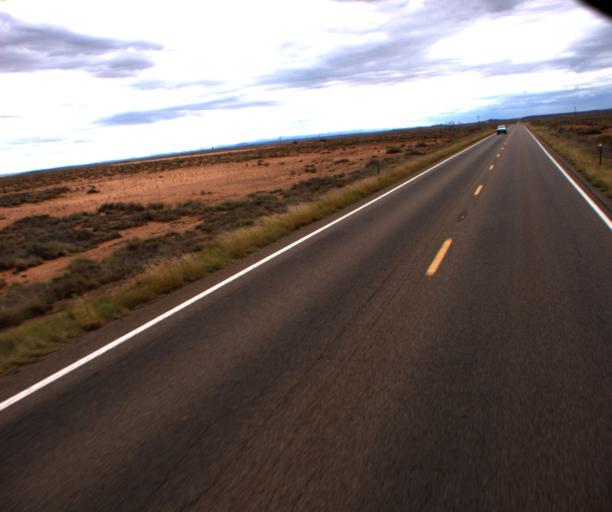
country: US
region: Arizona
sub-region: Navajo County
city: Holbrook
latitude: 34.8043
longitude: -110.1364
